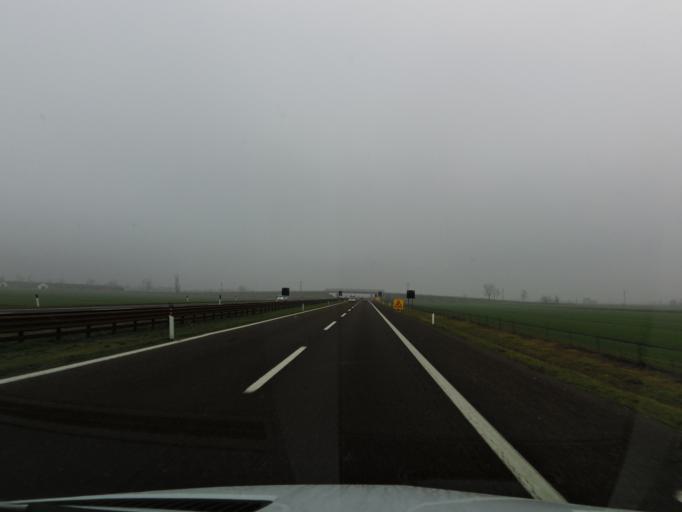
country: IT
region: Emilia-Romagna
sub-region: Provincia di Reggio Emilia
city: Rolo
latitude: 44.8516
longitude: 10.8519
